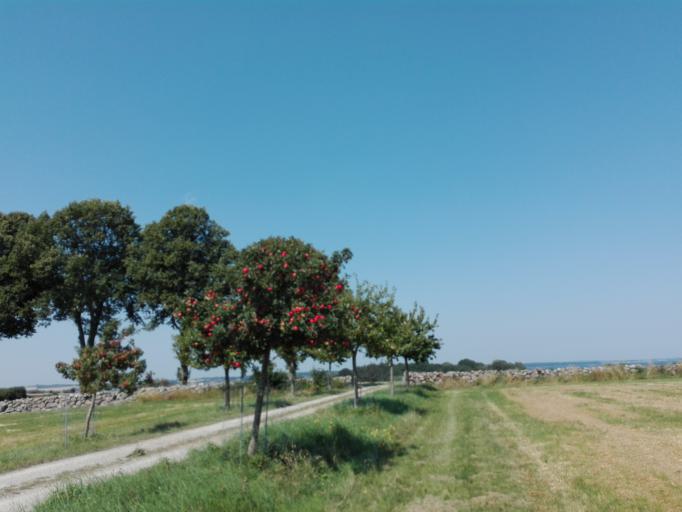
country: DK
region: Central Jutland
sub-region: Hedensted Kommune
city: Juelsminde
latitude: 55.7478
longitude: 10.0460
